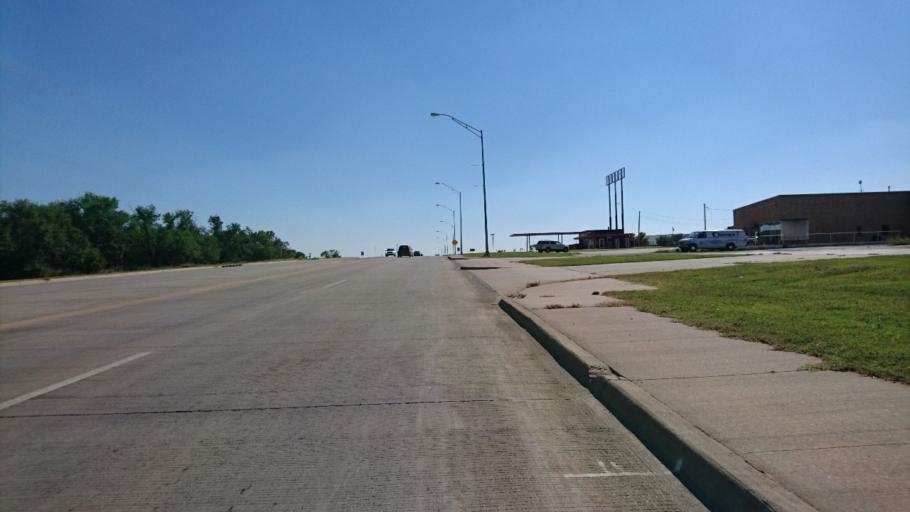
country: US
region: Oklahoma
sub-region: Custer County
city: Clinton
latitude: 35.5082
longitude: -98.9649
